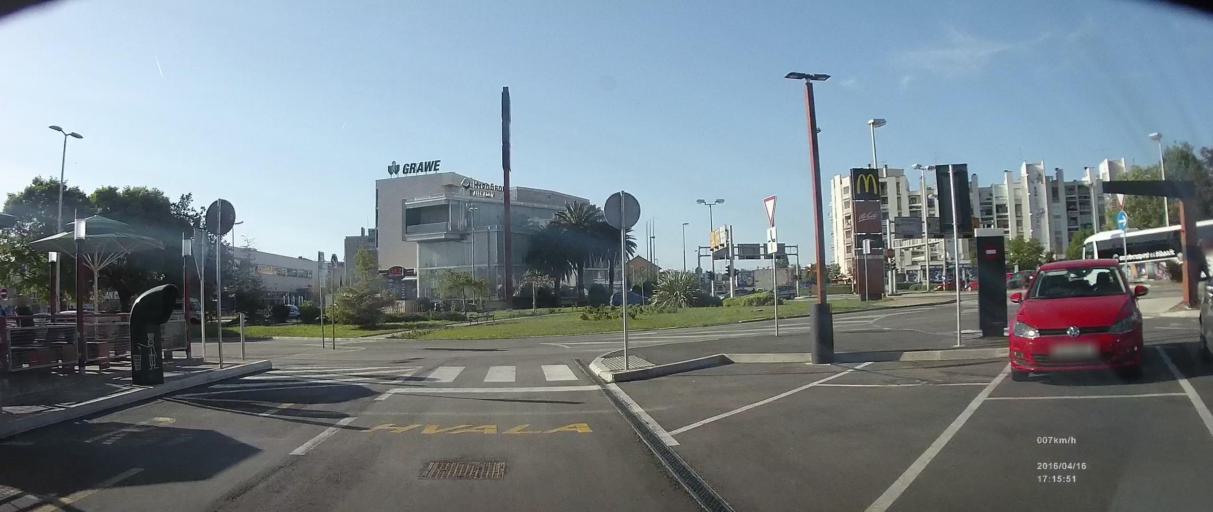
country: HR
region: Zadarska
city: Zadar
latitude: 44.1068
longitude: 15.2425
